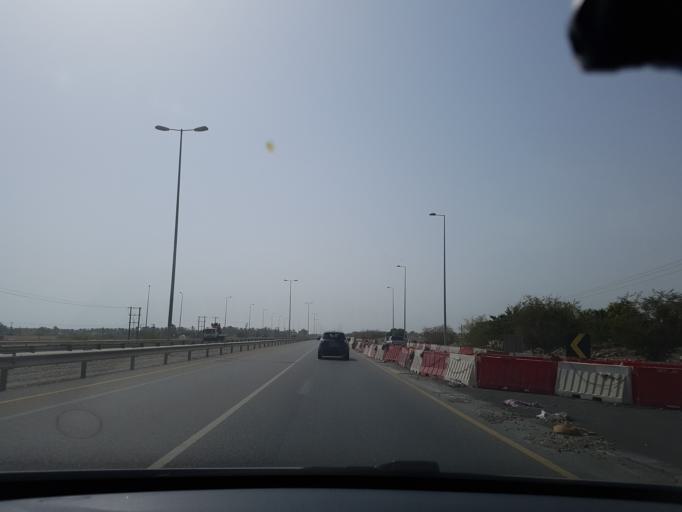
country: OM
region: Al Batinah
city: Al Khaburah
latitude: 23.9984
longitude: 57.0612
